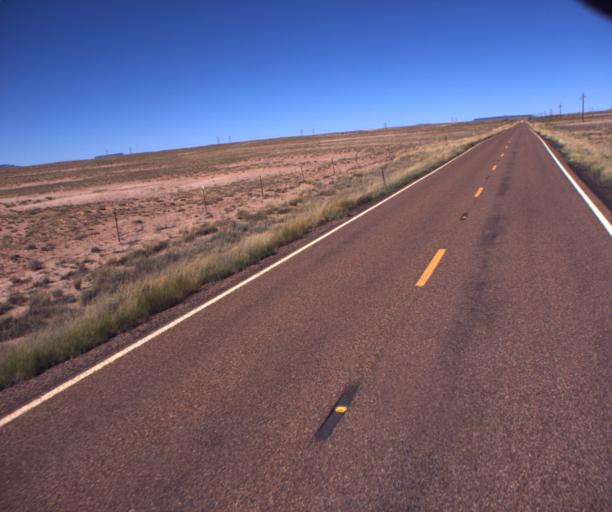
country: US
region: Arizona
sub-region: Navajo County
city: Holbrook
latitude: 35.1237
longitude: -110.0922
